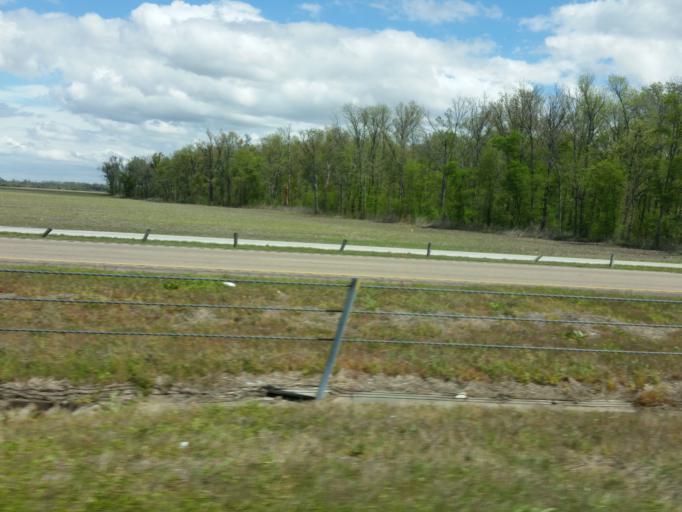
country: US
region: Arkansas
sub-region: Crittenden County
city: Marion
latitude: 35.3596
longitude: -90.2793
